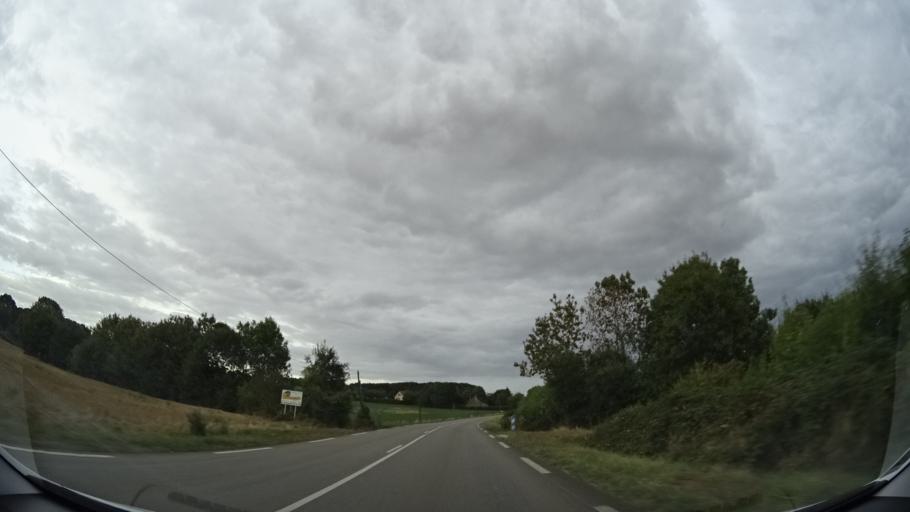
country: FR
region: Centre
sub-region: Departement du Loiret
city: Douchy
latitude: 47.9352
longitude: 3.0904
